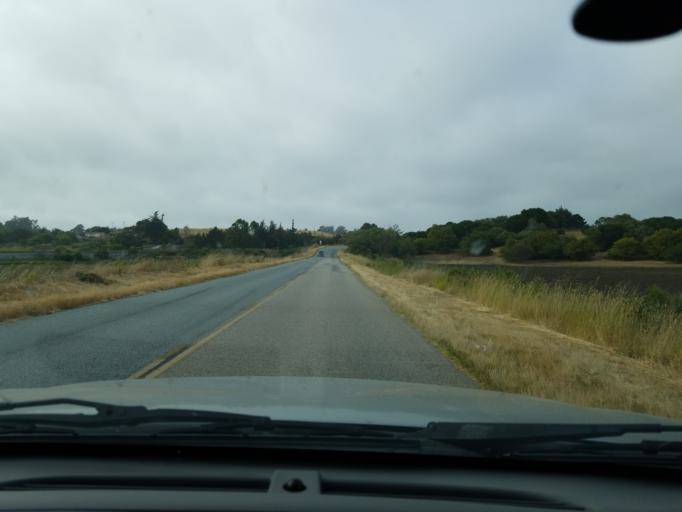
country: US
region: California
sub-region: Monterey County
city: Las Lomas
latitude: 36.8570
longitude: -121.7549
